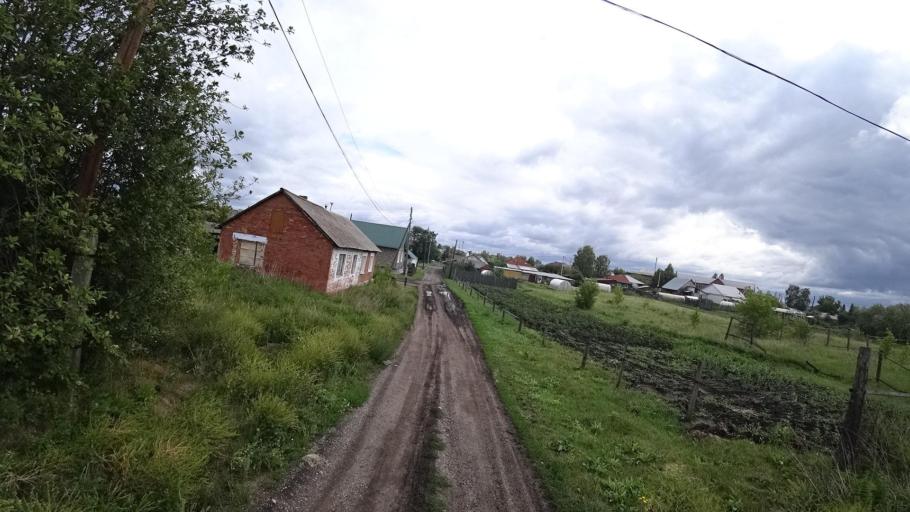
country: RU
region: Sverdlovsk
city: Kamyshlov
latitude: 56.8564
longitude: 62.6962
